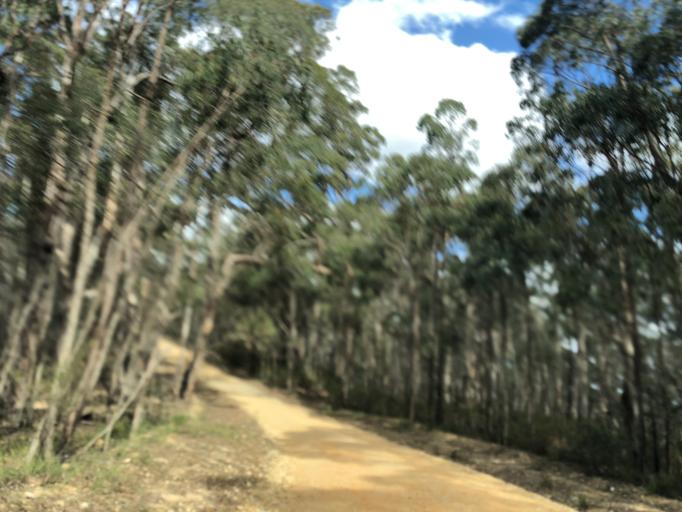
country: AU
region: Victoria
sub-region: Moorabool
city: Bacchus Marsh
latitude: -37.5358
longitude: 144.3331
